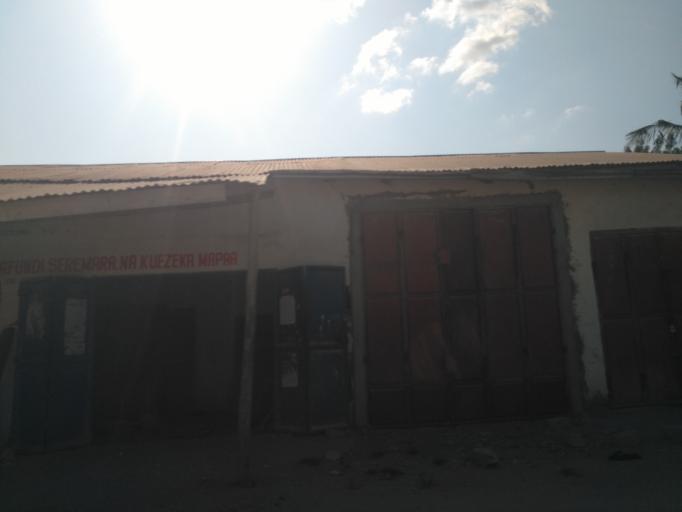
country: TZ
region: Dar es Salaam
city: Dar es Salaam
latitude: -6.8667
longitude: 39.3108
